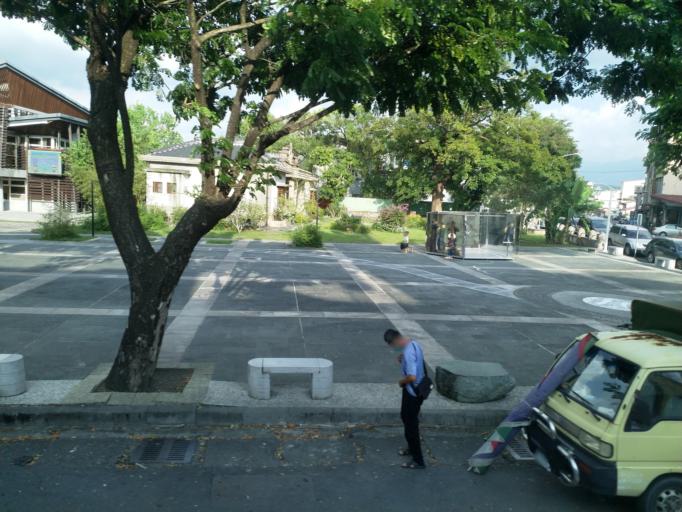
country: TW
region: Taiwan
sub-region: Pingtung
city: Pingtung
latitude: 22.8999
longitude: 120.5420
